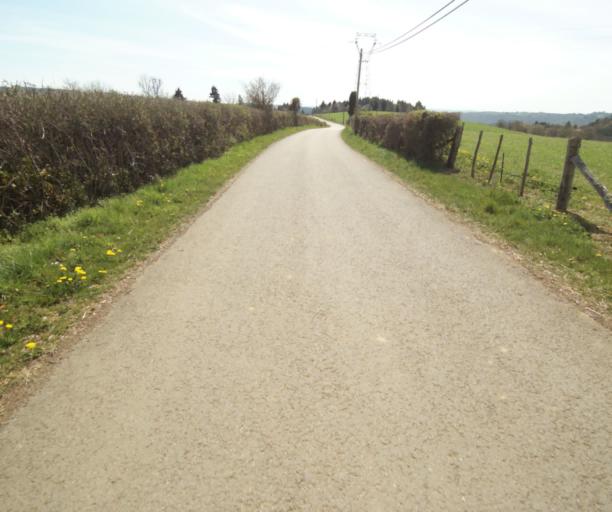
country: FR
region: Limousin
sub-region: Departement de la Correze
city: Naves
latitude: 45.3684
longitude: 1.8027
